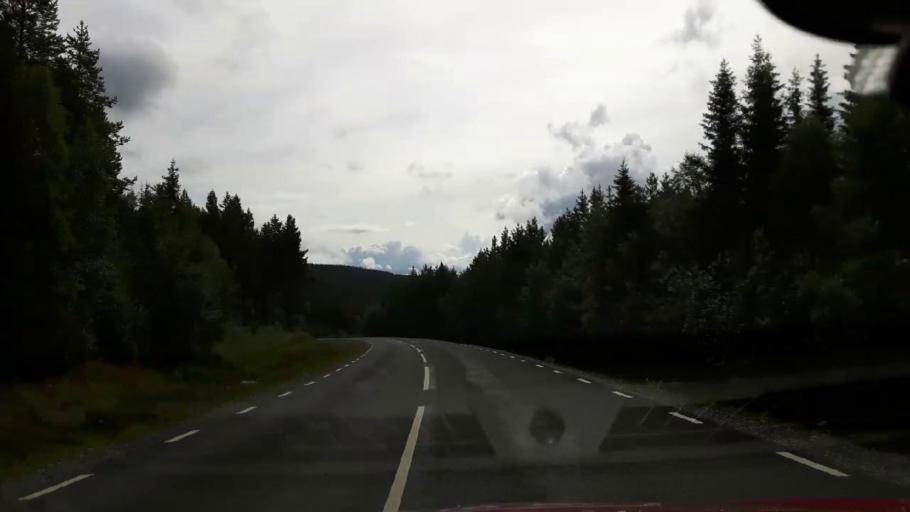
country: NO
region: Nord-Trondelag
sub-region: Lierne
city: Sandvika
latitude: 64.6379
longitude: 14.1370
